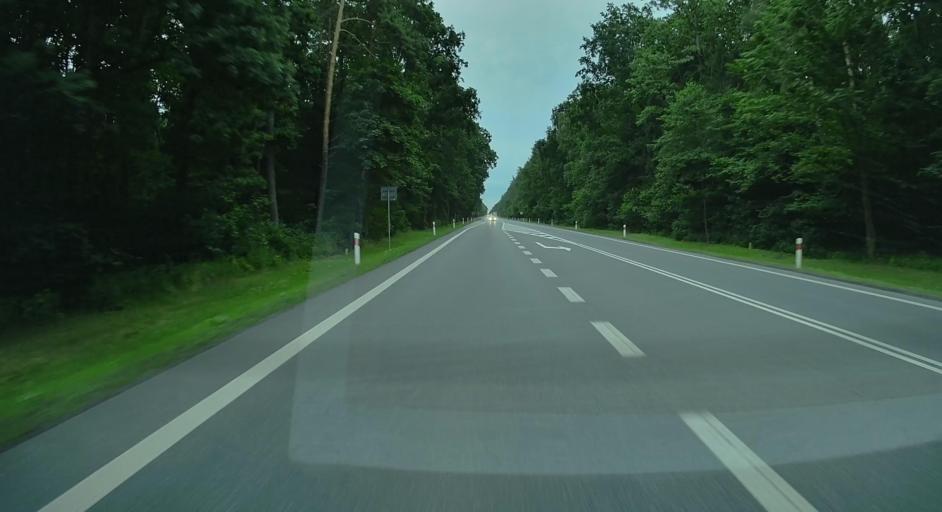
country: PL
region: Lublin Voivodeship
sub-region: Powiat bialski
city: Zalesie
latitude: 52.0357
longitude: 23.3946
